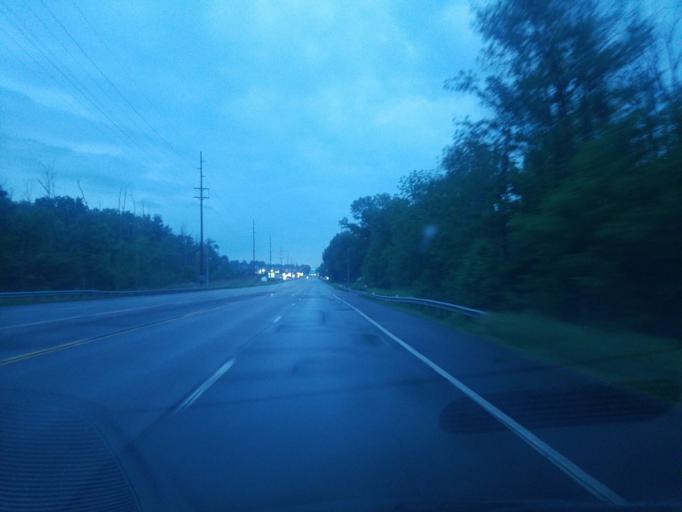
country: US
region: Ohio
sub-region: Mahoning County
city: Boardman
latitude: 41.0247
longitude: -80.6979
